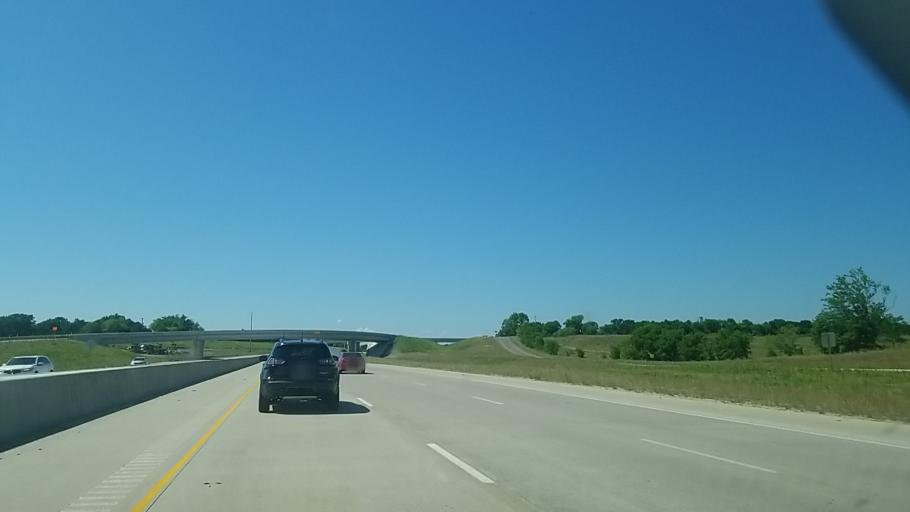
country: US
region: Texas
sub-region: Navarro County
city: Corsicana
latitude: 32.1494
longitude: -96.4659
